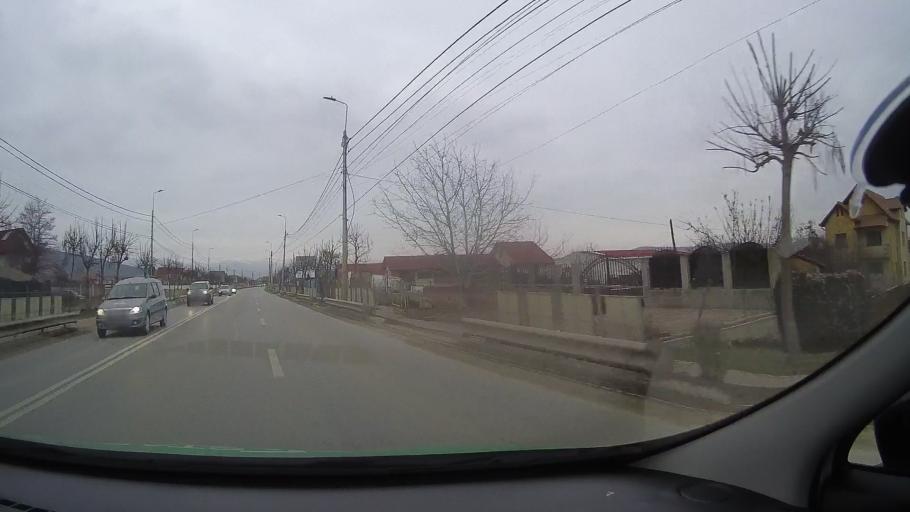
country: RO
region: Alba
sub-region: Municipiul Alba Iulia
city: Micesti
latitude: 46.0950
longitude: 23.5533
